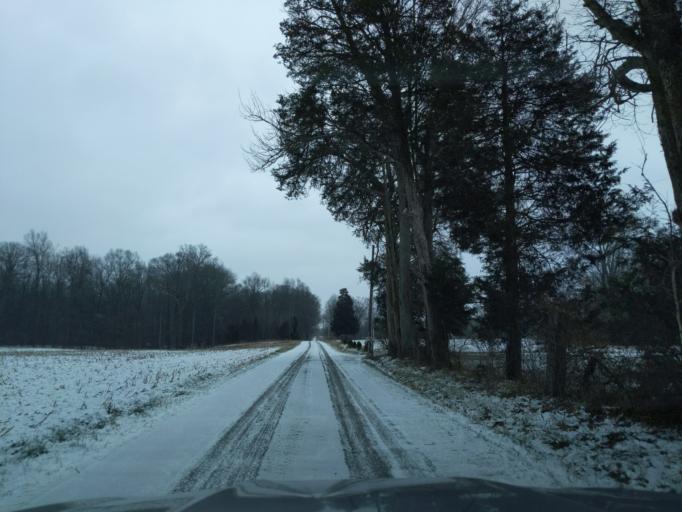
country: US
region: Indiana
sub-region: Decatur County
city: Westport
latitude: 39.2049
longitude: -85.5052
